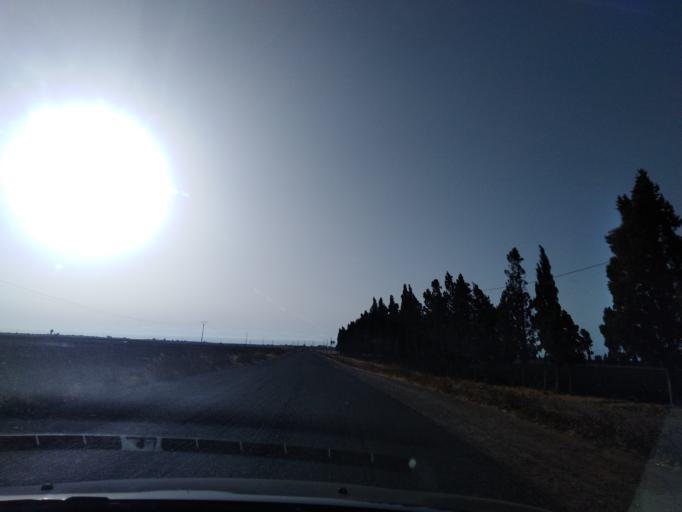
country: MA
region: Doukkala-Abda
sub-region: Safi
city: Safi
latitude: 32.4897
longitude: -8.9227
